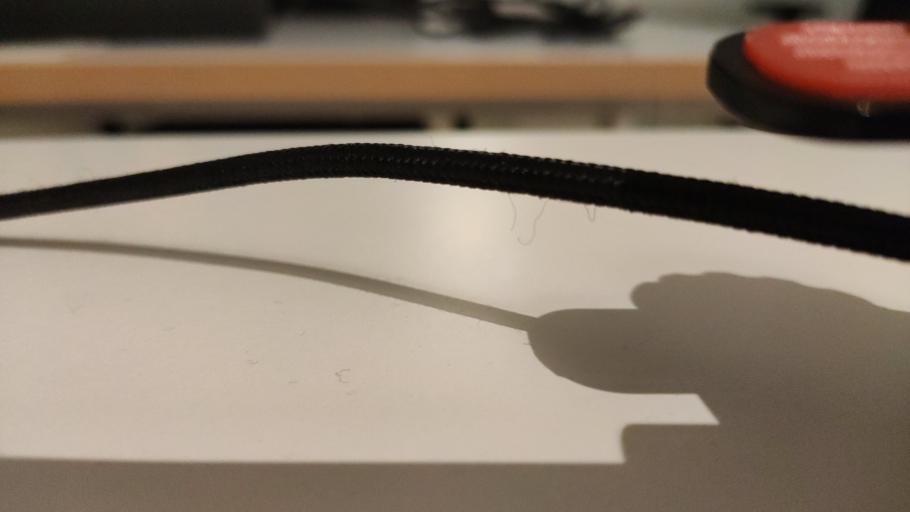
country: RU
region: Moskovskaya
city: Rogachevo
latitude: 56.4338
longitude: 37.1806
